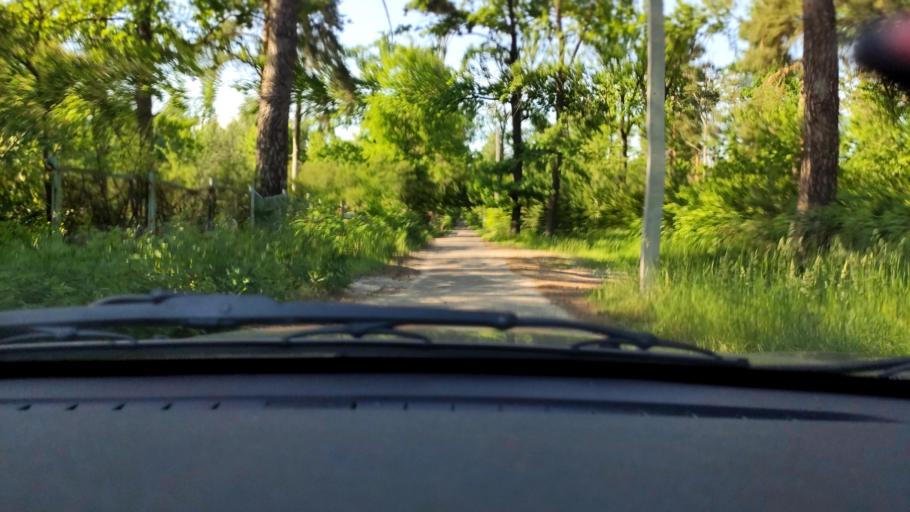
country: RU
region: Voronezj
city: Somovo
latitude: 51.7520
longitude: 39.3744
